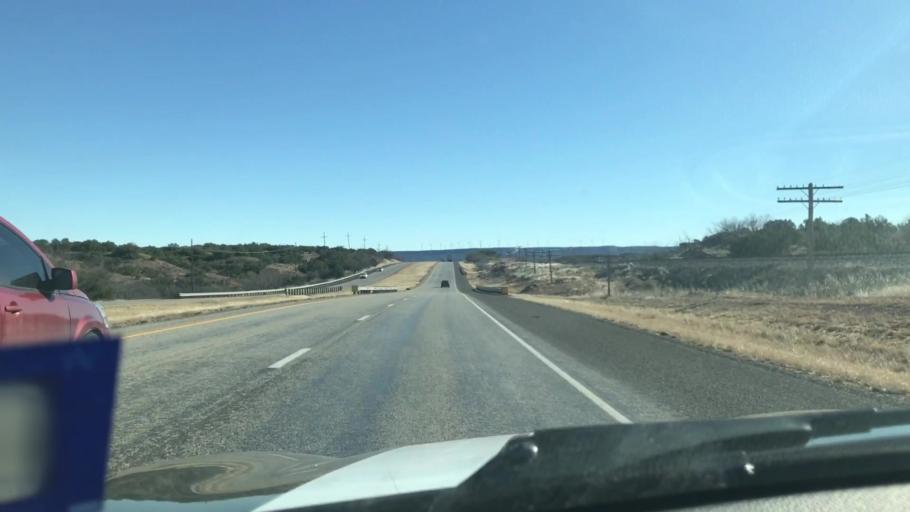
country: US
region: Texas
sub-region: Garza County
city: Post
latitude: 33.0254
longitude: -101.1841
